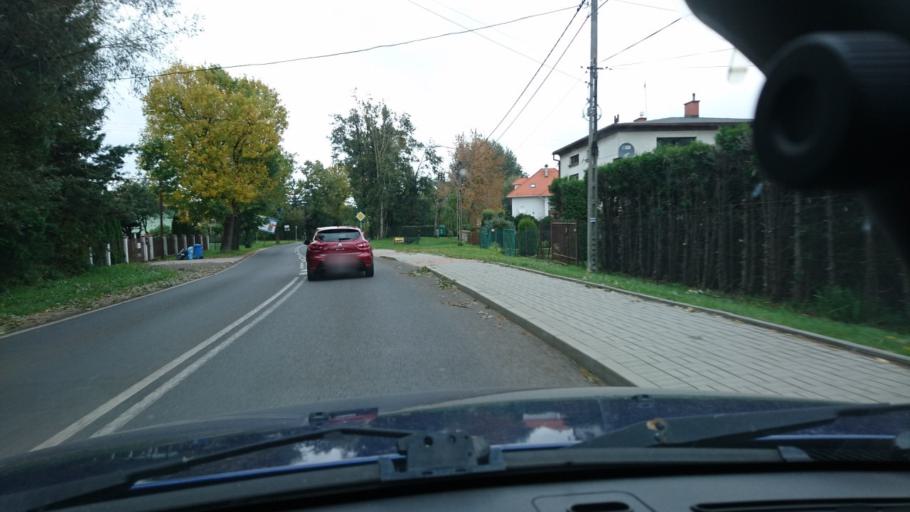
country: PL
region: Silesian Voivodeship
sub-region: Powiat bielski
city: Jaworze
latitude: 49.8051
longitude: 18.9819
